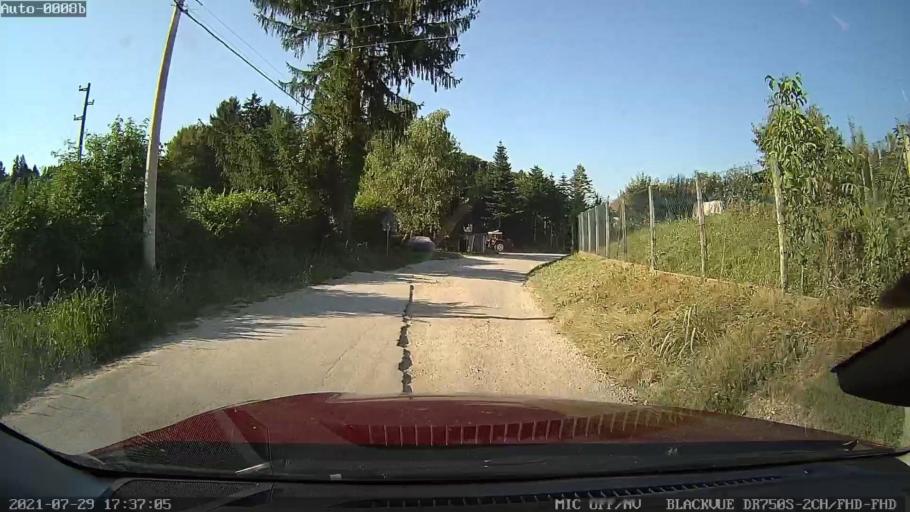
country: HR
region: Varazdinska
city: Vinica
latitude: 46.3075
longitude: 16.1569
